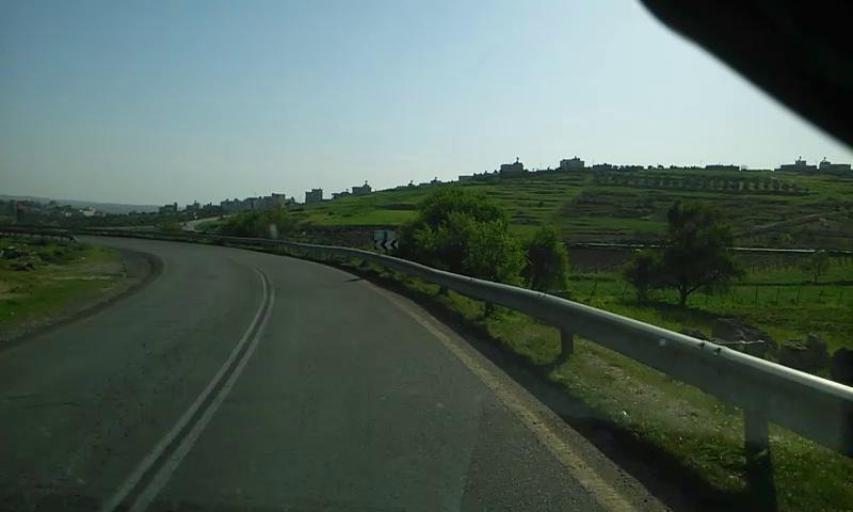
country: PS
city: Al Hilah
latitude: 31.4726
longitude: 35.1325
